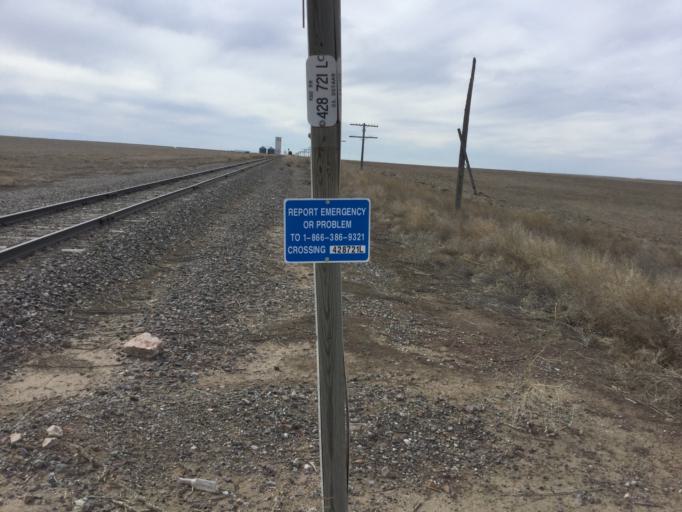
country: US
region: Kansas
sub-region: Greeley County
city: Tribune
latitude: 38.4726
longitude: -101.9561
